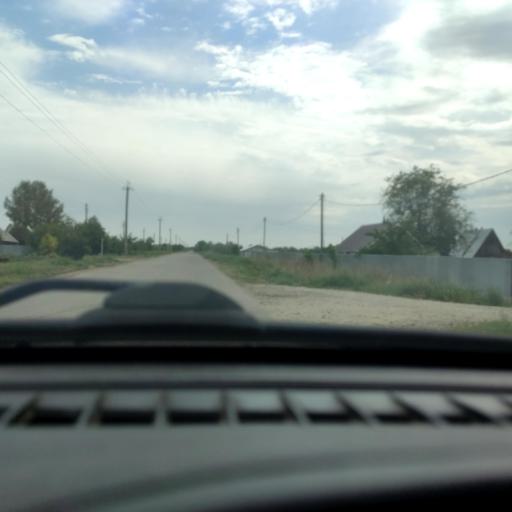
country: RU
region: Samara
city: Tol'yatti
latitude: 53.6433
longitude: 49.3307
